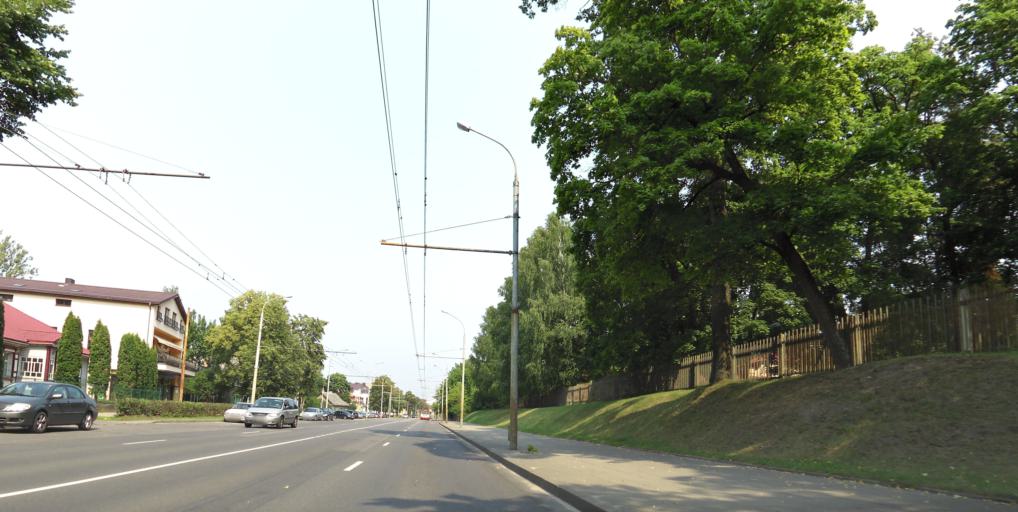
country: LT
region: Vilnius County
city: Rasos
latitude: 54.6973
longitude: 25.3087
